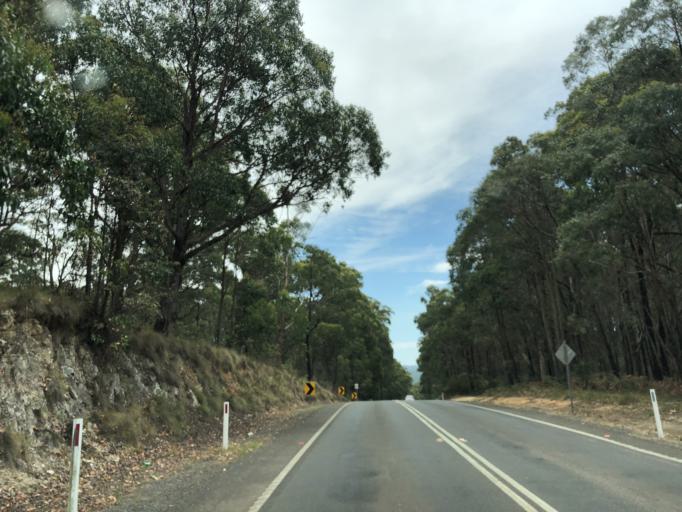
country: AU
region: Victoria
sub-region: Moorabool
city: Bacchus Marsh
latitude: -37.4920
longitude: 144.3063
